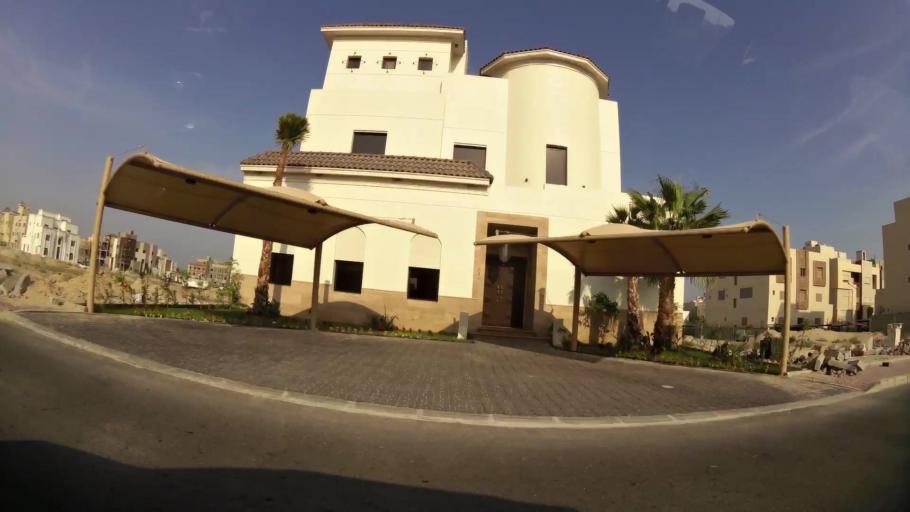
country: KW
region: Mubarak al Kabir
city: Mubarak al Kabir
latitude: 29.1930
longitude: 48.1056
